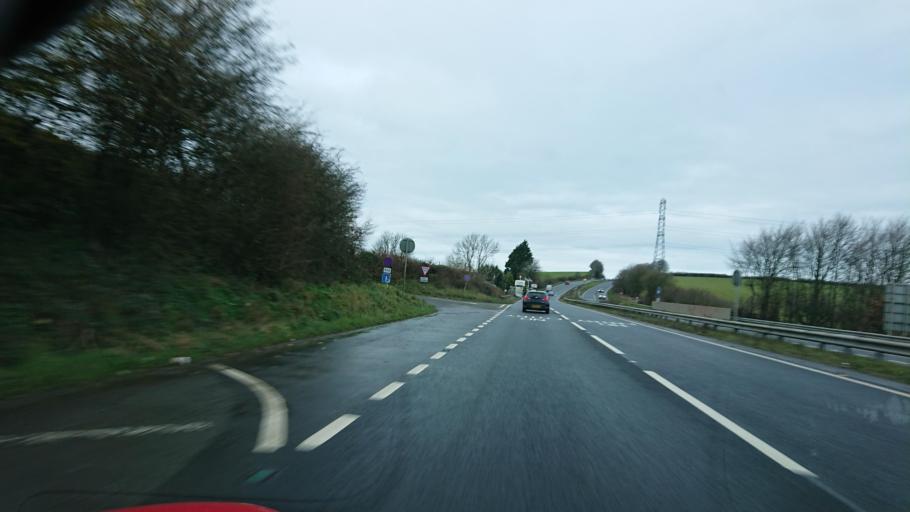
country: GB
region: England
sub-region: Cornwall
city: Liskeard
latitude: 50.4342
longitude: -4.4386
